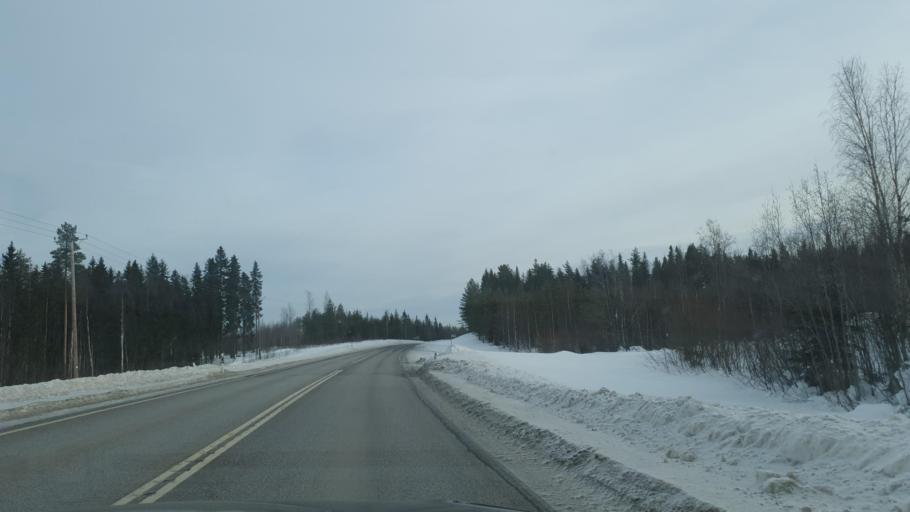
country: FI
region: Kainuu
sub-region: Kajaani
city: Vaala
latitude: 64.5315
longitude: 27.2611
